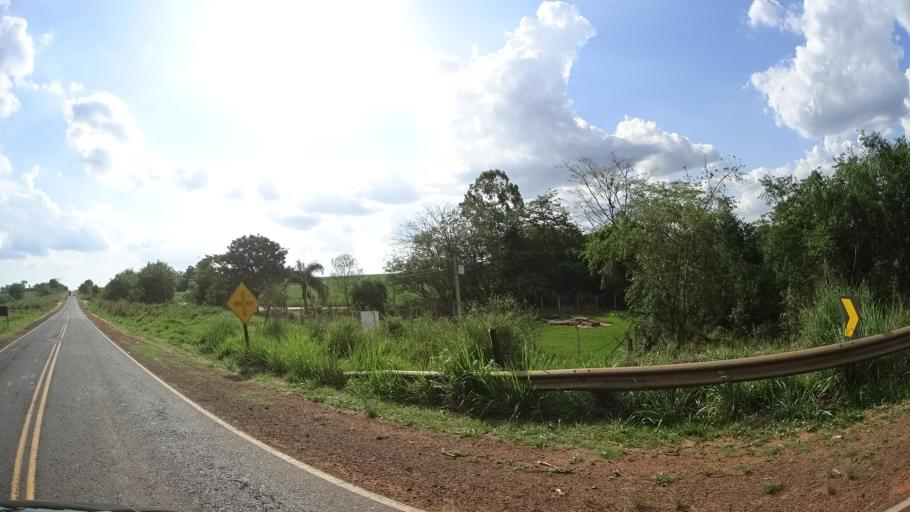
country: BR
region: Sao Paulo
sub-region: Urupes
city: Urupes
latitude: -21.1959
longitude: -49.3136
